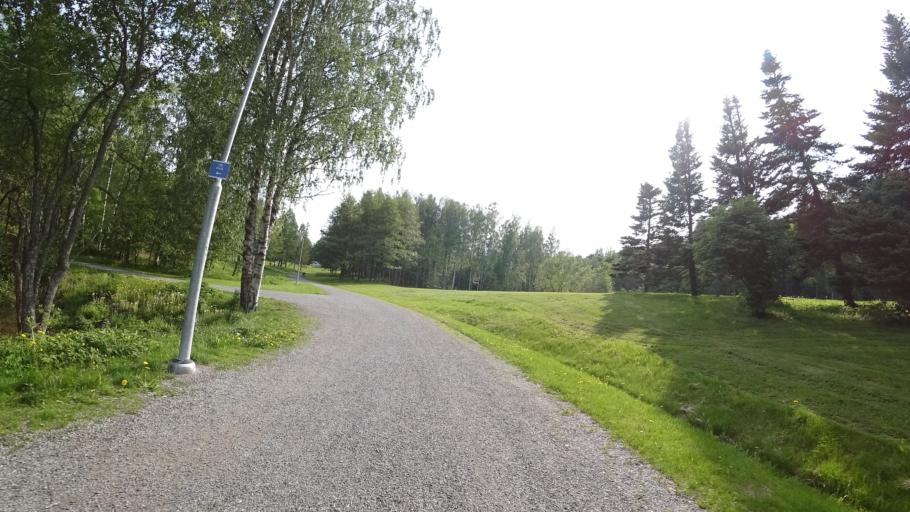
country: FI
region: Pirkanmaa
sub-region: Tampere
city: Pirkkala
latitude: 61.5043
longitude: 23.6637
